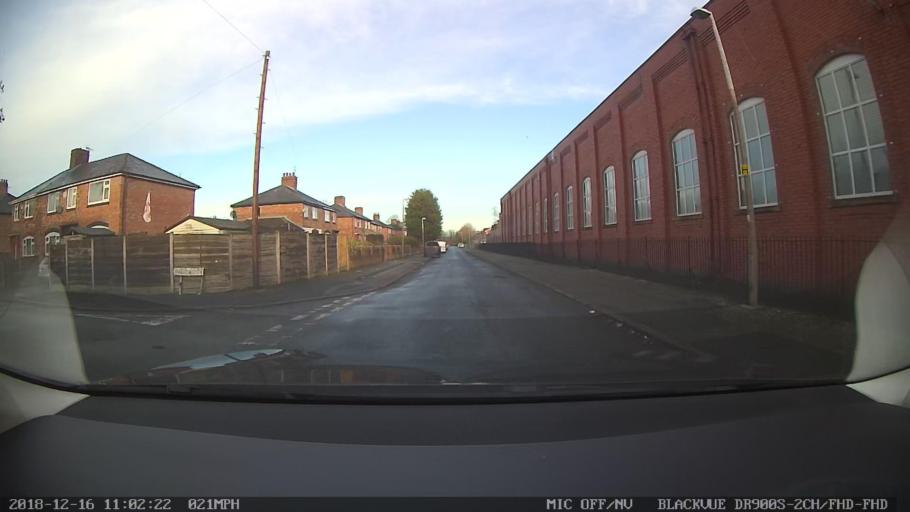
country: GB
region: England
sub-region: Manchester
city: Swinton
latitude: 53.4788
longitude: -2.3698
